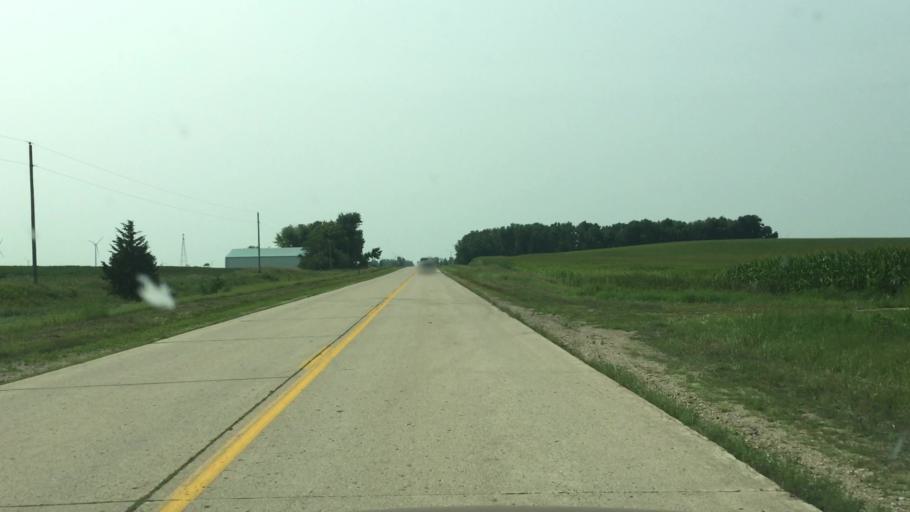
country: US
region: Iowa
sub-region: Dickinson County
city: Lake Park
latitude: 43.4234
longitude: -95.2891
